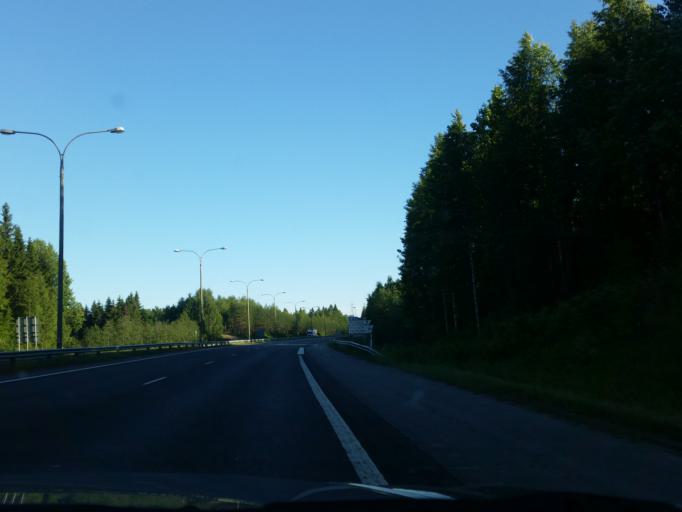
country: FI
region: Northern Savo
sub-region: Kuopio
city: Kuopio
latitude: 62.8537
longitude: 27.6210
